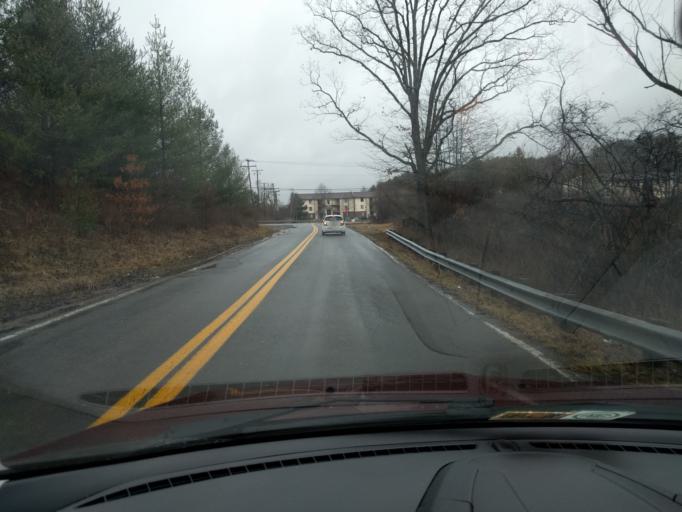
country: US
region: West Virginia
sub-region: Raleigh County
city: Mabscott
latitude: 37.7994
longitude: -81.2079
